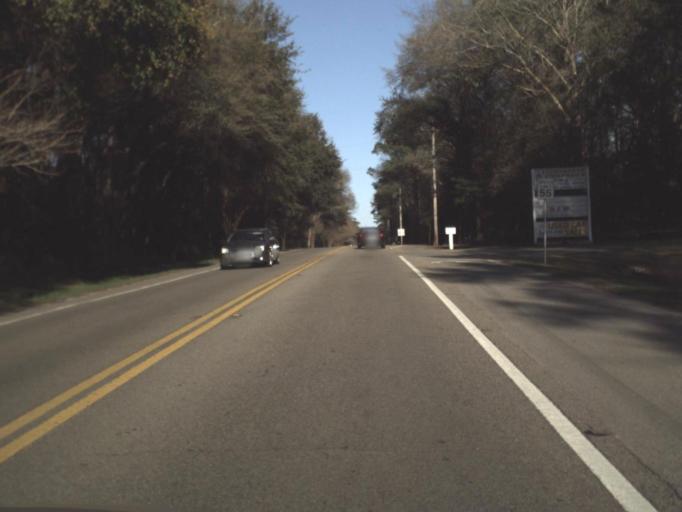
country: US
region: Florida
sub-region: Leon County
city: Tallahassee
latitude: 30.4882
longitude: -84.1474
